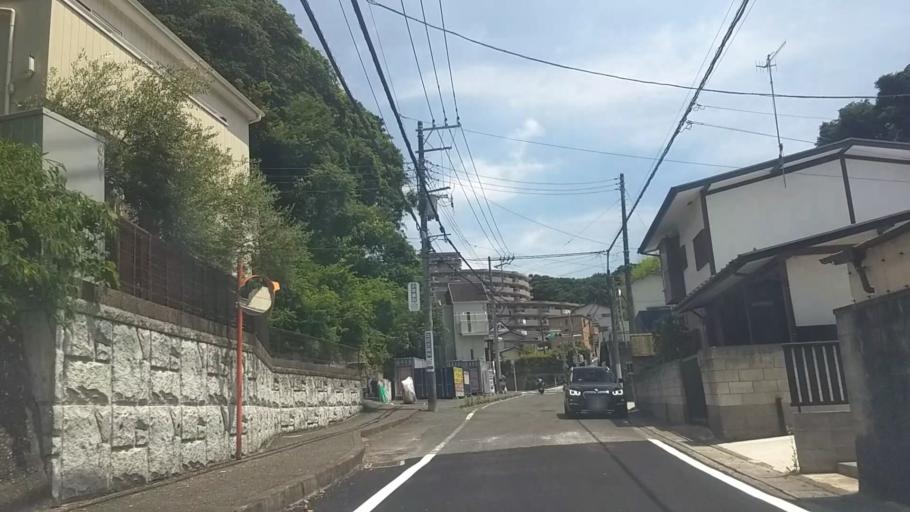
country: JP
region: Kanagawa
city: Zushi
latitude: 35.3000
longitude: 139.5643
